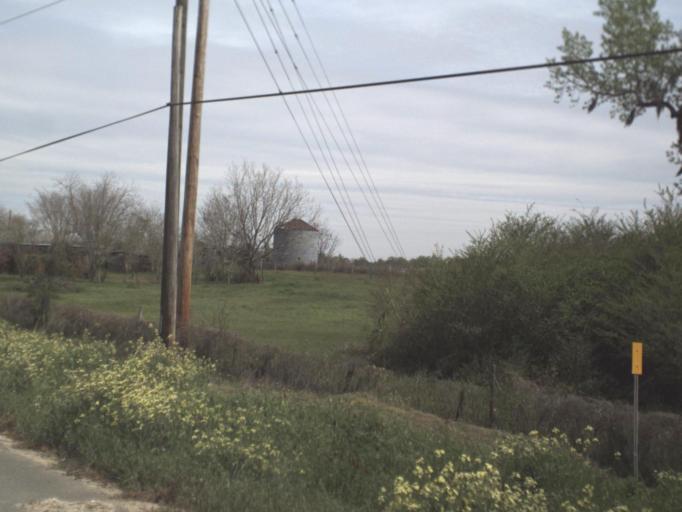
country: US
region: Florida
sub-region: Jackson County
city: Graceville
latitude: 30.9385
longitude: -85.4138
